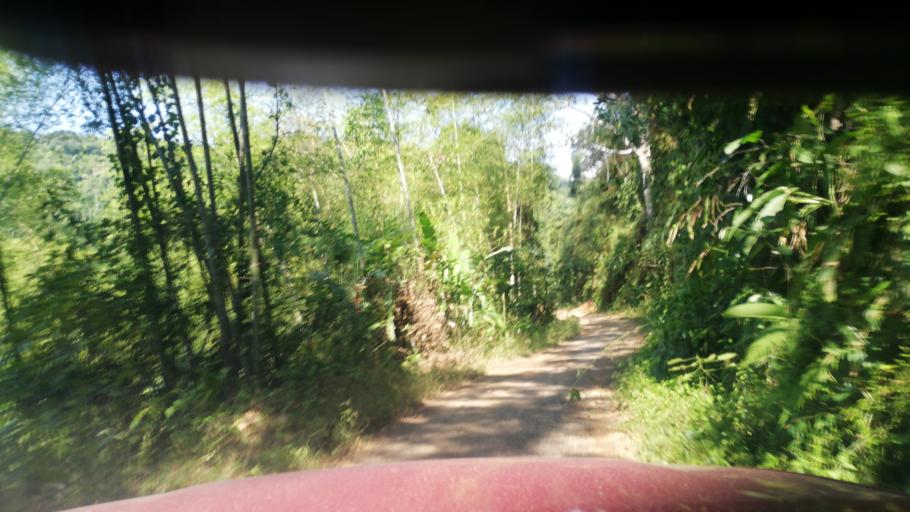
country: CO
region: Risaralda
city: Balboa
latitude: 4.9040
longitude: -75.9415
